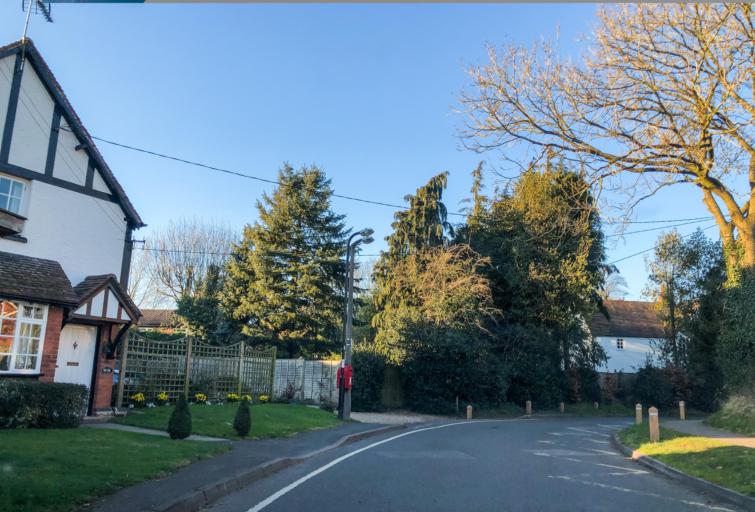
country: GB
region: England
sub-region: Warwickshire
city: Wroxall
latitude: 52.3043
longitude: -1.6595
